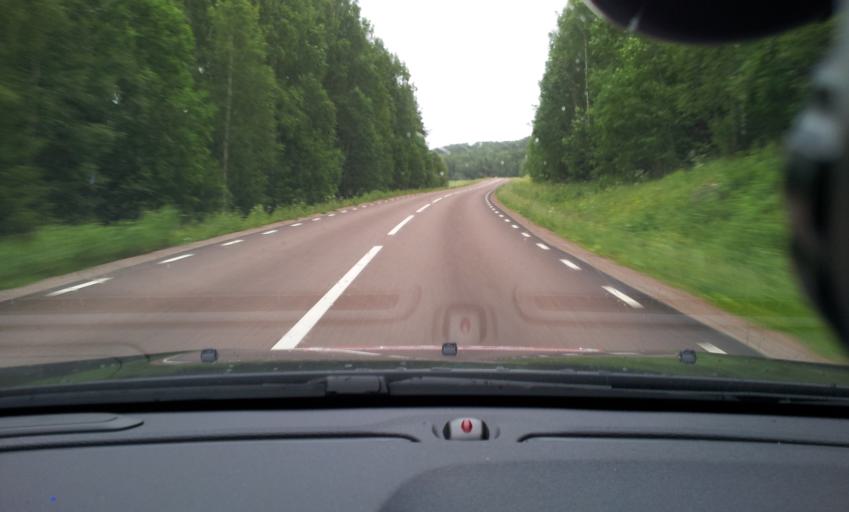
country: SE
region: Jaemtland
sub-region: Ragunda Kommun
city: Hammarstrand
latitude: 63.0583
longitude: 16.4734
